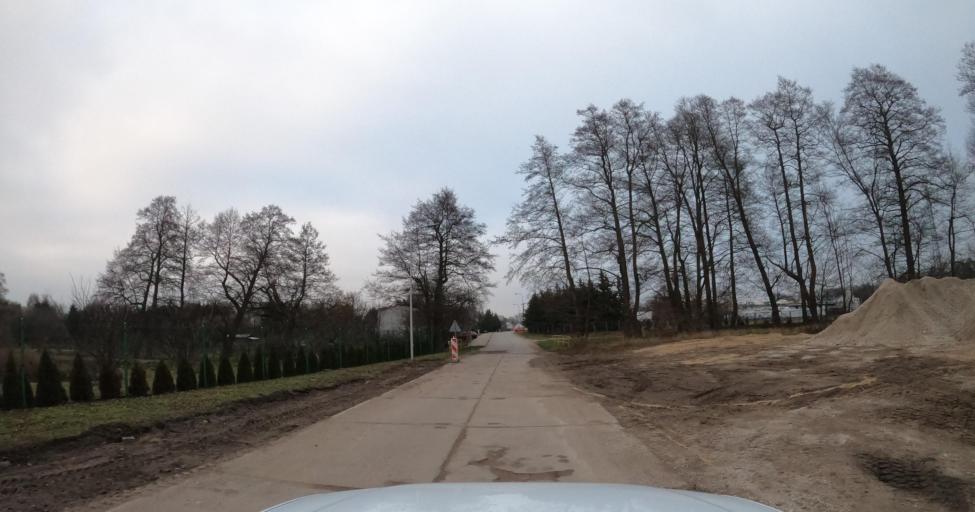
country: PL
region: West Pomeranian Voivodeship
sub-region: Powiat walecki
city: Miroslawiec
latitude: 53.3357
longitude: 16.0887
